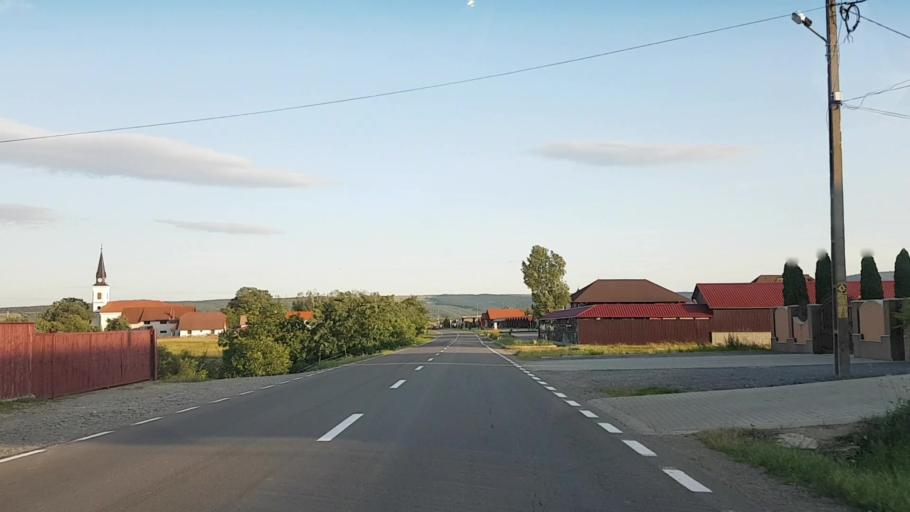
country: RO
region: Harghita
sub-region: Comuna Lupeni
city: Lupeni
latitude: 46.3796
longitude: 25.2193
